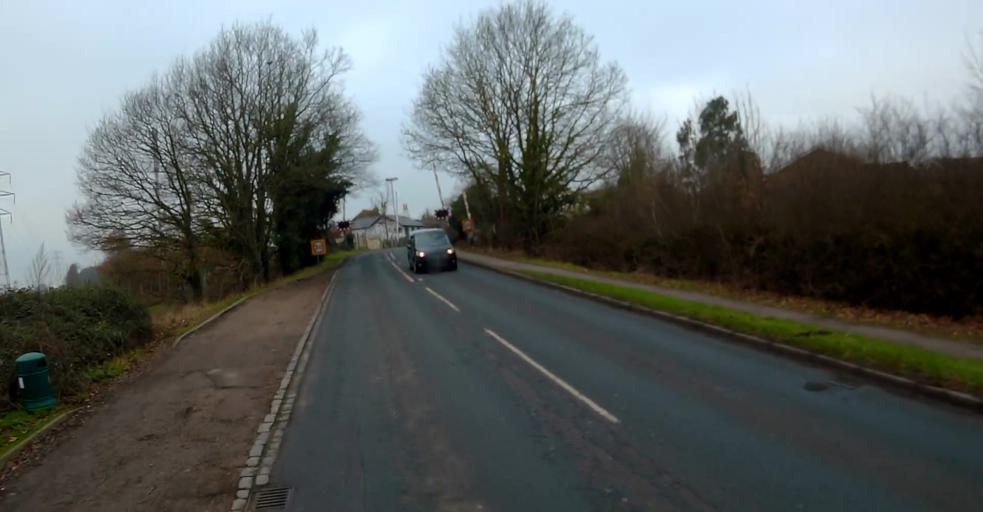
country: GB
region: England
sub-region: Wokingham
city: Wokingham
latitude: 51.4039
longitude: -0.8194
